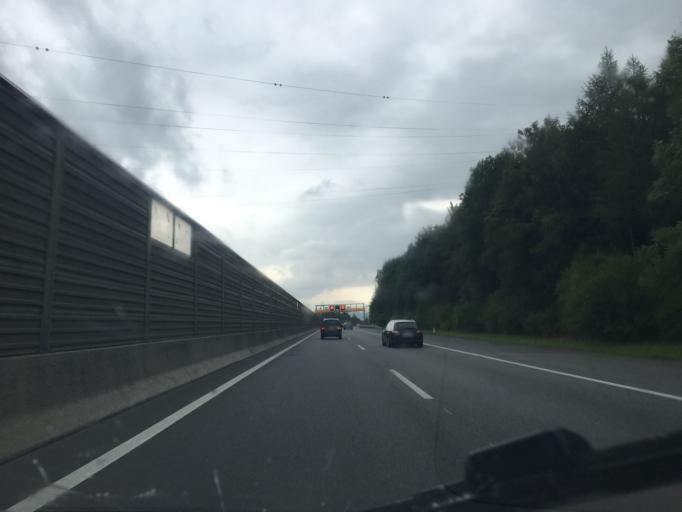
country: AT
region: Tyrol
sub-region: Politischer Bezirk Innsbruck Land
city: Hall in Tirol
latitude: 47.2734
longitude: 11.5018
